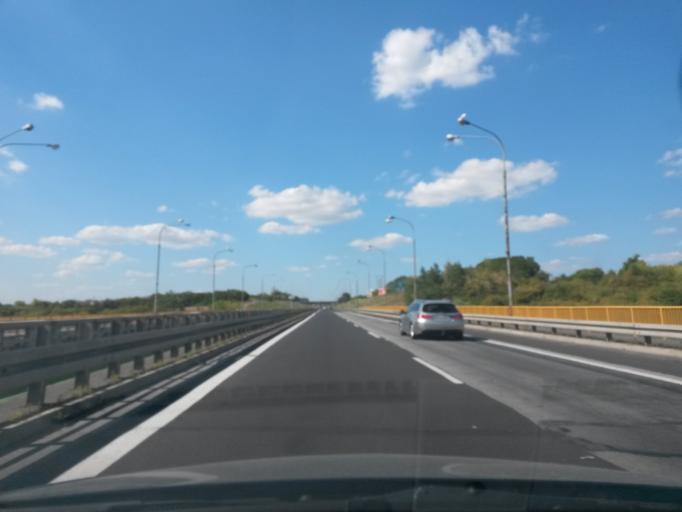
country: PL
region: Masovian Voivodeship
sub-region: Powiat nowodworski
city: Zakroczym
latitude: 52.4283
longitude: 20.6548
